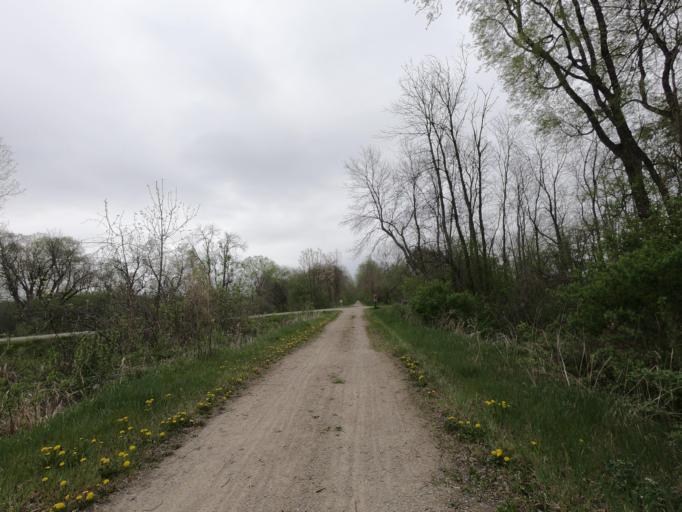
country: US
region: Wisconsin
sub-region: Jefferson County
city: Johnson Creek
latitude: 43.0280
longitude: -88.7396
